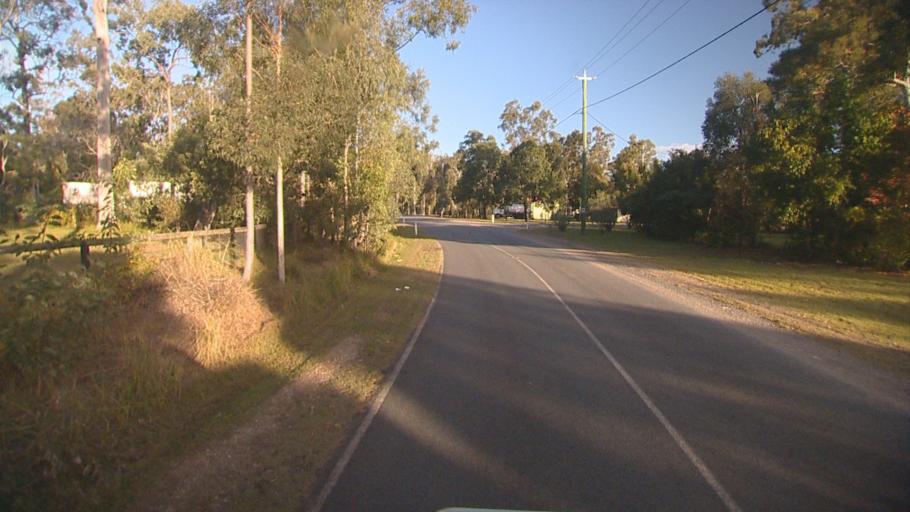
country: AU
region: Queensland
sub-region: Logan
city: Waterford West
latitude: -27.7317
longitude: 153.1375
